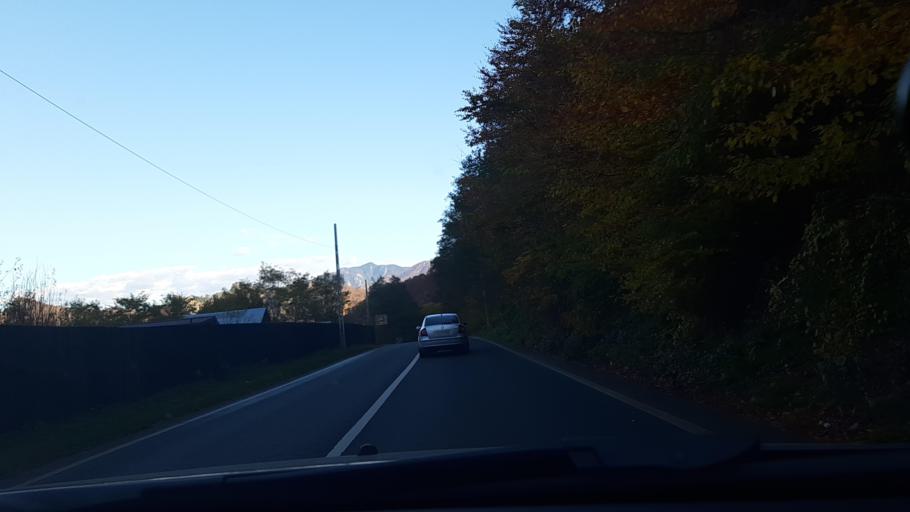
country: RO
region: Valcea
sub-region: Comuna Brezoi
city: Brezoi
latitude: 45.3435
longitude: 24.2144
